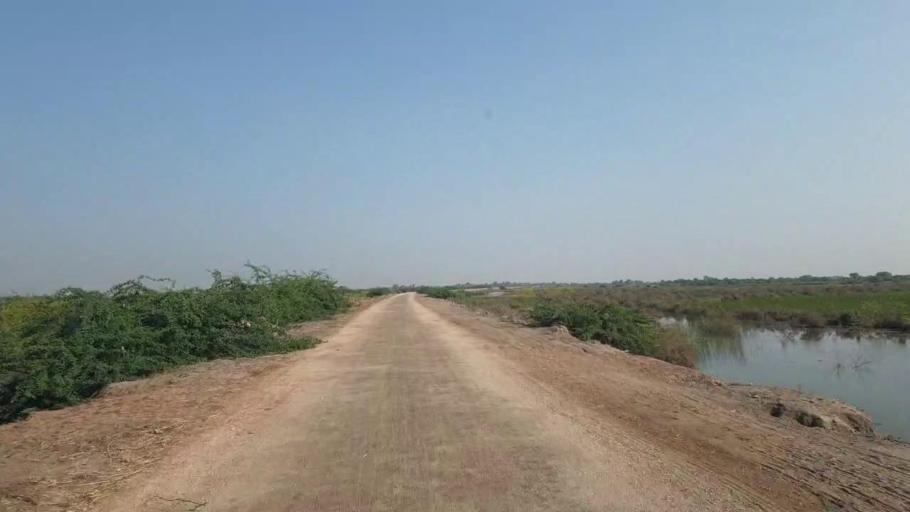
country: PK
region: Sindh
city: Badin
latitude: 24.4834
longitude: 68.7460
